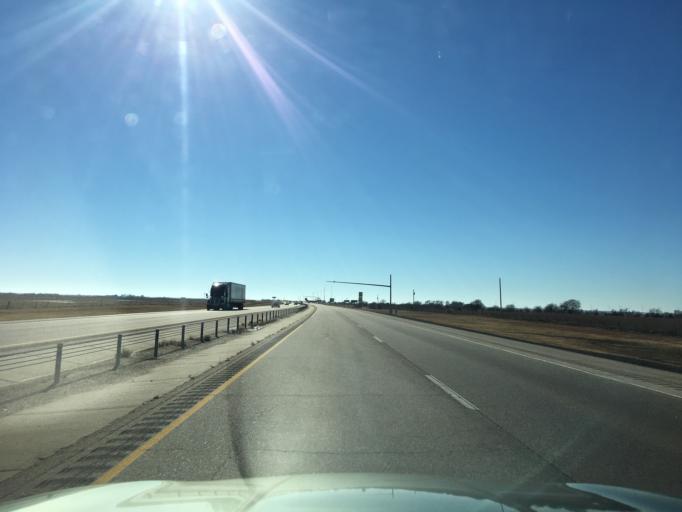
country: US
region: Oklahoma
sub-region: Kay County
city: Blackwell
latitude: 36.9959
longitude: -97.3437
